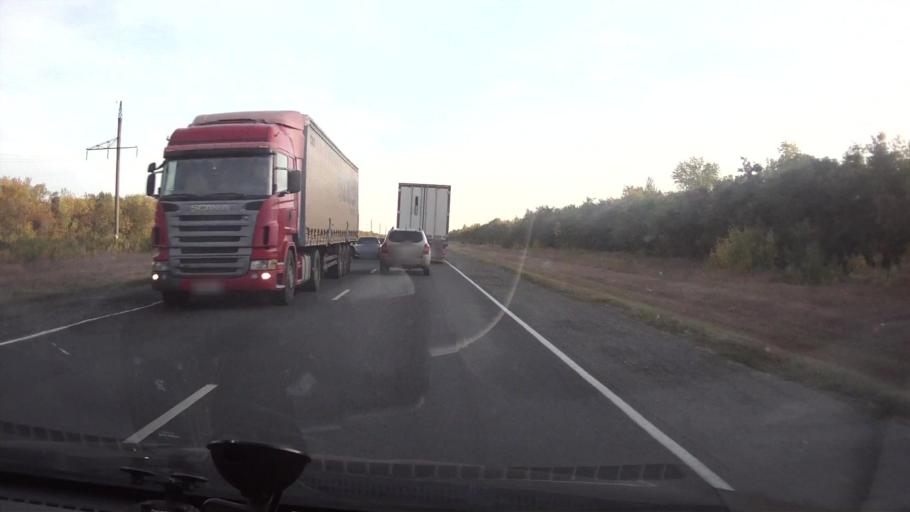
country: RU
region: Saratov
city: Krasnoarmeysk
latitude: 51.1249
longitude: 45.6506
